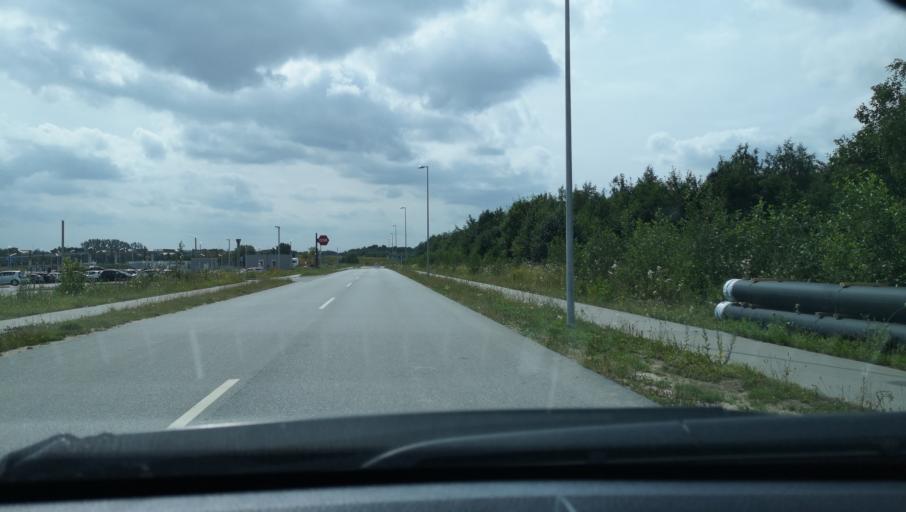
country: DK
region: Zealand
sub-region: Solrod Kommune
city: Solrod
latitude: 55.5011
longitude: 12.1710
